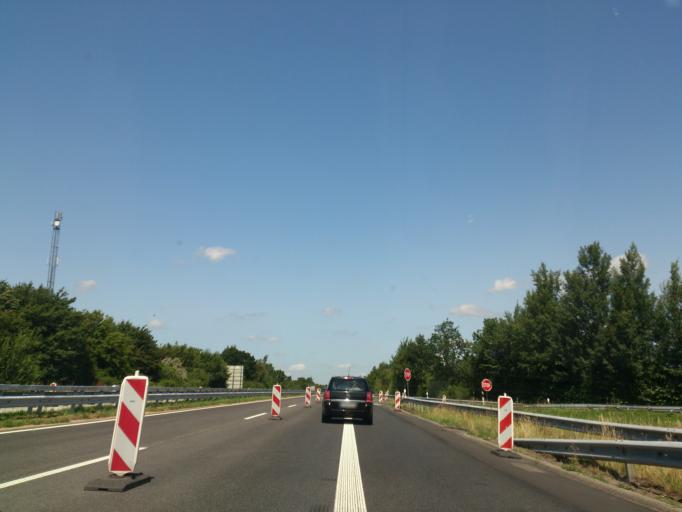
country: DE
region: Schleswig-Holstein
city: Tensbuttel-Rost
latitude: 54.1197
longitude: 9.2584
